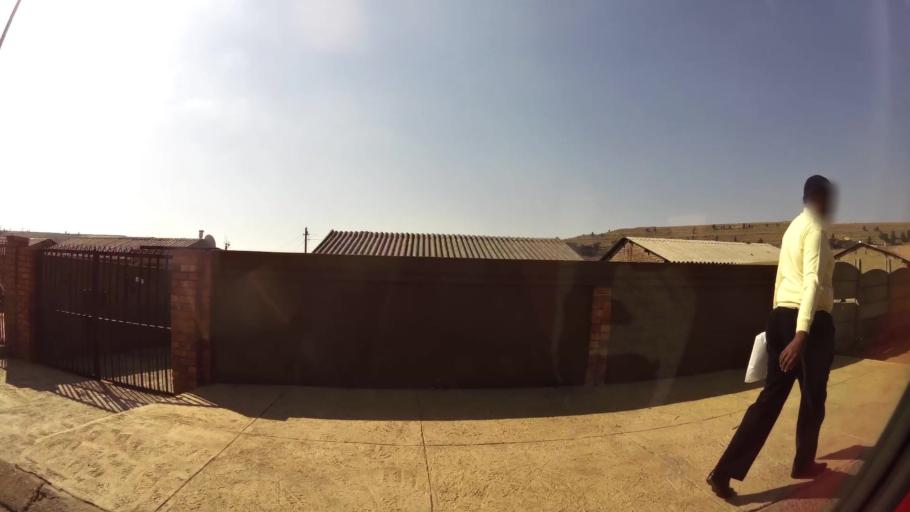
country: ZA
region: Gauteng
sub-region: City of Johannesburg Metropolitan Municipality
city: Johannesburg
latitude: -26.2383
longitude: 27.9575
